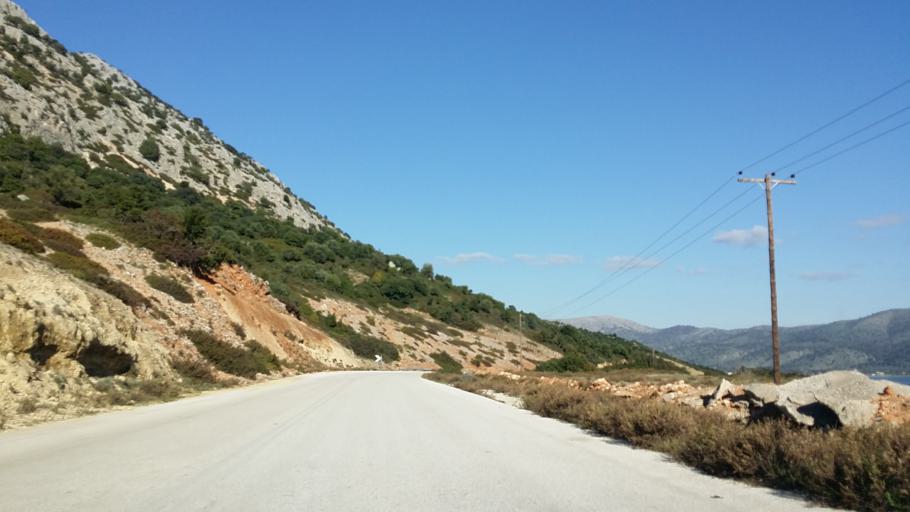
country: GR
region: West Greece
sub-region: Nomos Aitolias kai Akarnanias
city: Astakos
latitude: 38.5166
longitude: 21.0560
